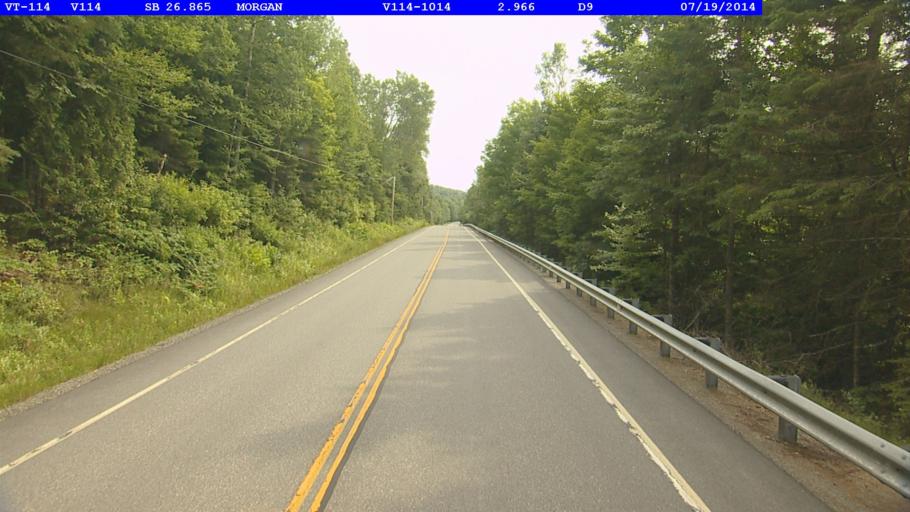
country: CA
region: Quebec
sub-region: Estrie
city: Coaticook
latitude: 44.8865
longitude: -71.8957
